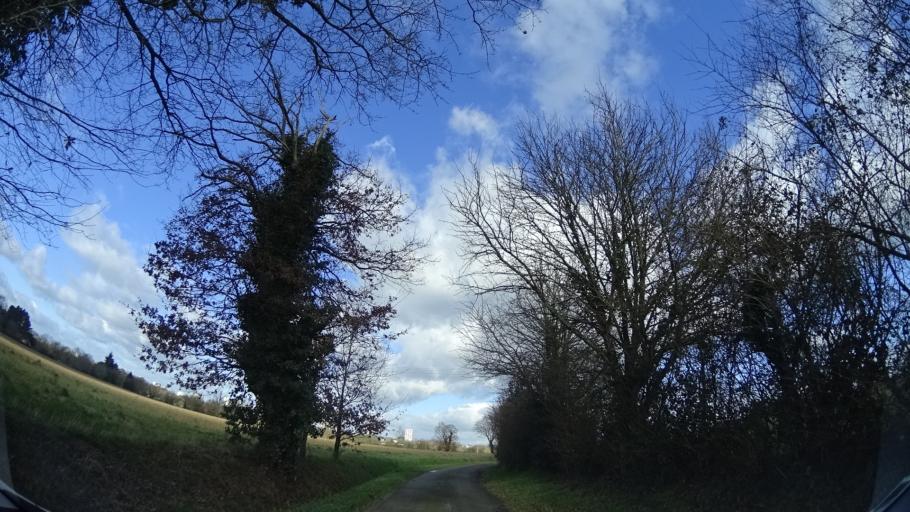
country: FR
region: Brittany
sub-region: Departement d'Ille-et-Vilaine
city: Chantepie
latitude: 48.0776
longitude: -1.6424
